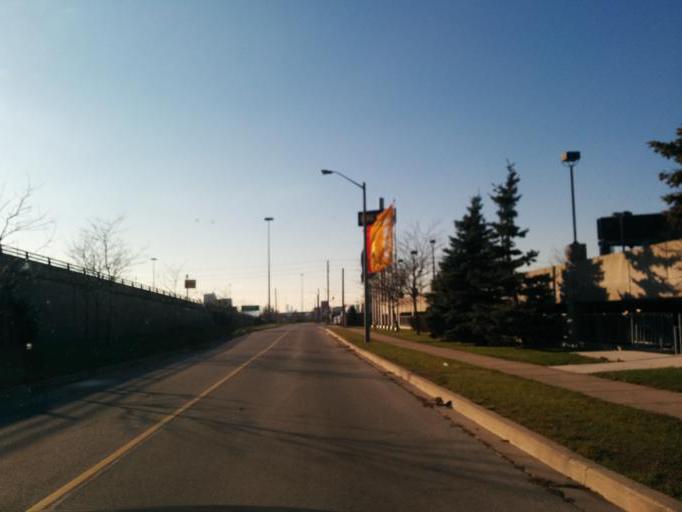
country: CA
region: Ontario
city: Etobicoke
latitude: 43.6167
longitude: -79.5342
